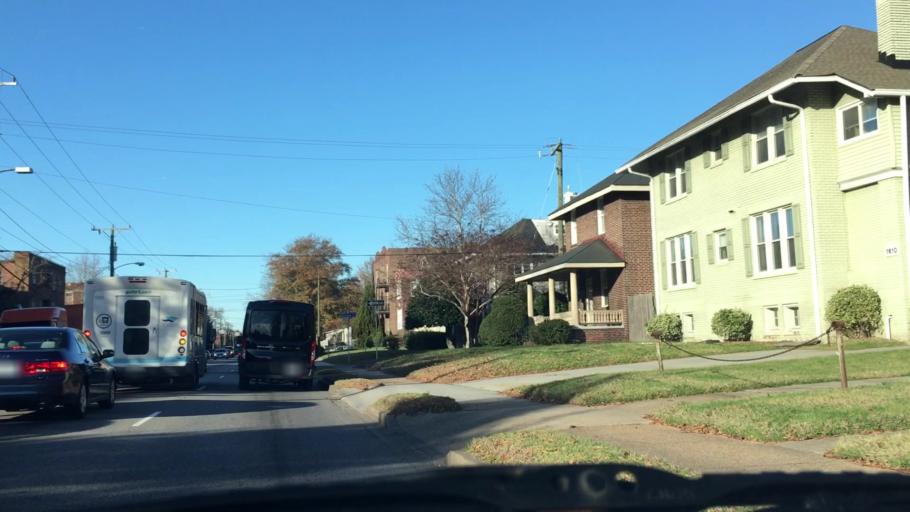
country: US
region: Virginia
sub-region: City of Norfolk
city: Norfolk
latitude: 36.8694
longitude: -76.3007
